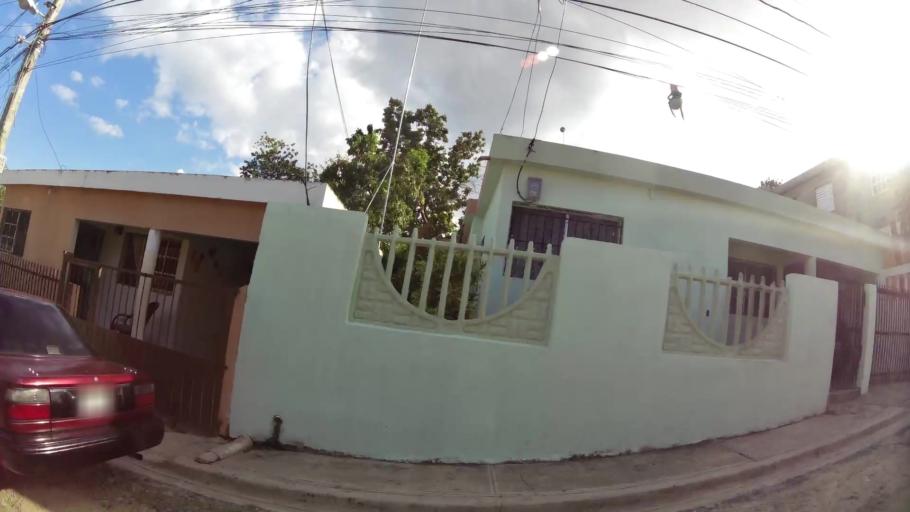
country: DO
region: Nacional
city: Ensanche Luperon
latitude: 18.5534
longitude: -69.8953
